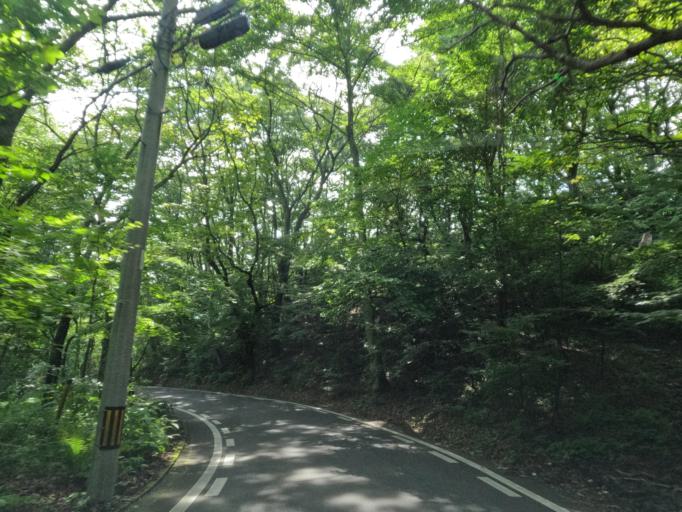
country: JP
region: Nagano
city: Komoro
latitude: 36.3574
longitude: 138.6096
